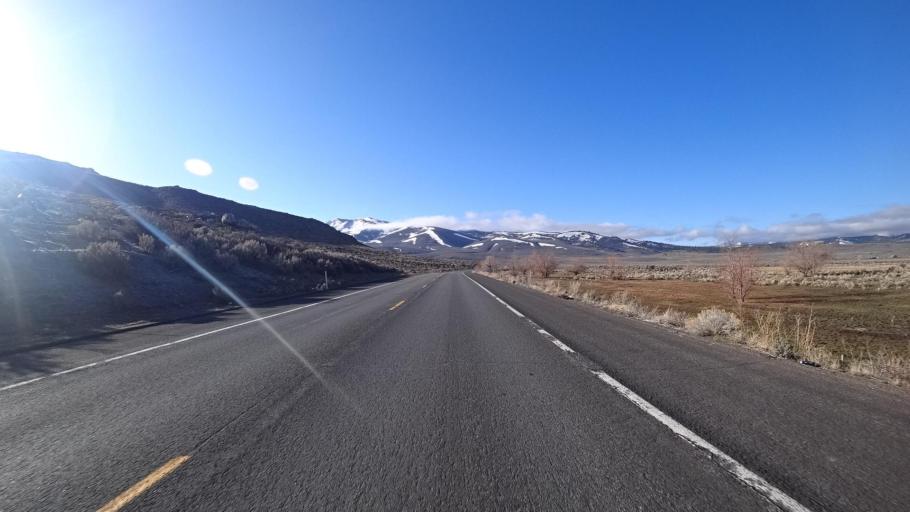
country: US
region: Nevada
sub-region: Washoe County
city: Cold Springs
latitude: 39.6551
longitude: -119.9585
